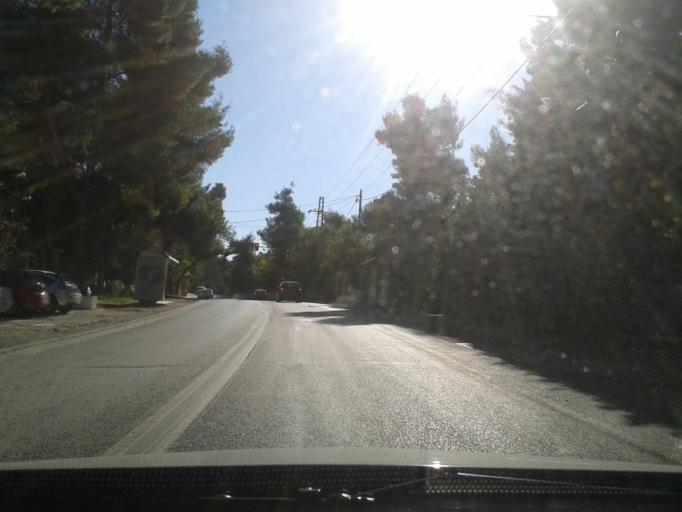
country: GR
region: Attica
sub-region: Nomarchia Anatolikis Attikis
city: Drosia
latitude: 38.1066
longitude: 23.8643
